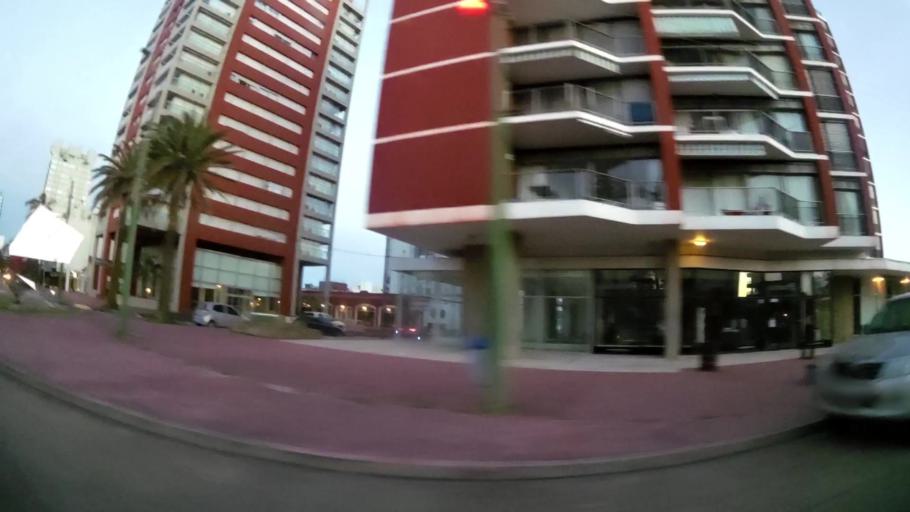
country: UY
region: Maldonado
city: Punta del Este
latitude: -34.9664
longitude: -54.9483
